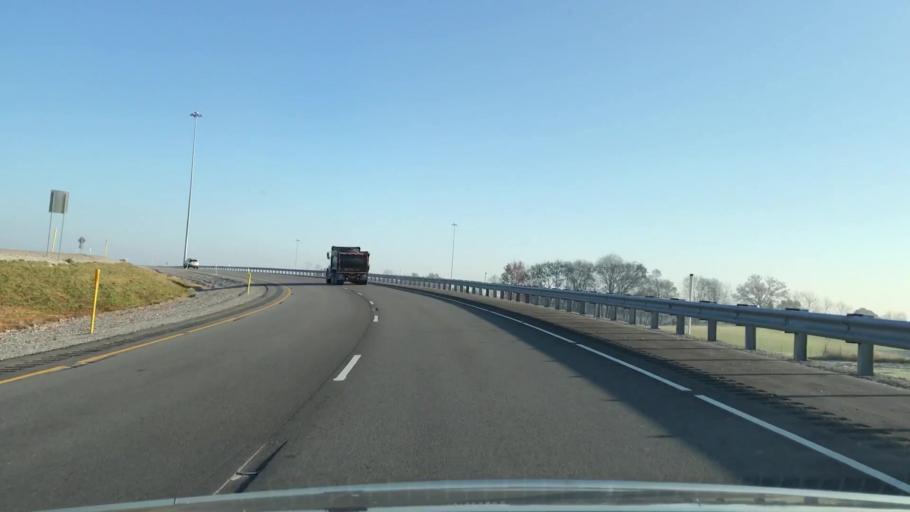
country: US
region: Kentucky
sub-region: Warren County
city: Bowling Green
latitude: 37.0096
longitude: -86.3281
